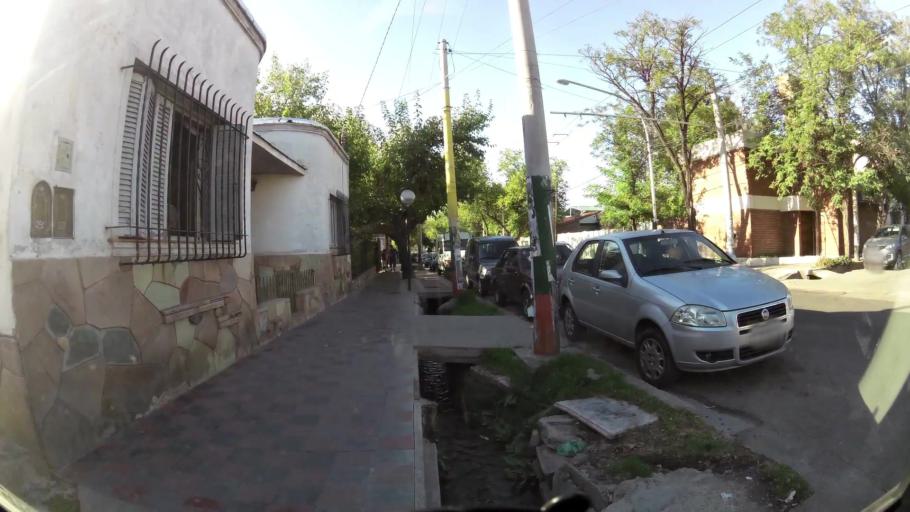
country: AR
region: Mendoza
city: Mendoza
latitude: -32.8994
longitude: -68.8287
